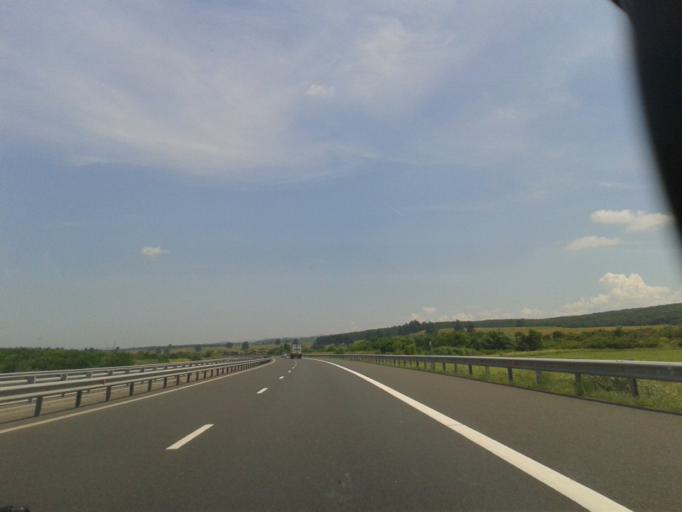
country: RO
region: Hunedoara
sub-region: Comuna Turdas
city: Turdas
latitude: 45.8375
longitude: 23.0979
